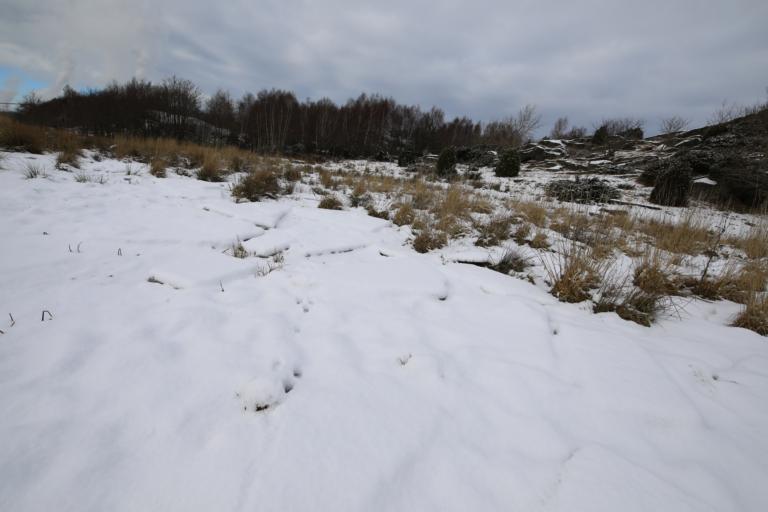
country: SE
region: Halland
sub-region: Kungsbacka Kommun
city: Frillesas
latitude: 57.2246
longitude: 12.2005
